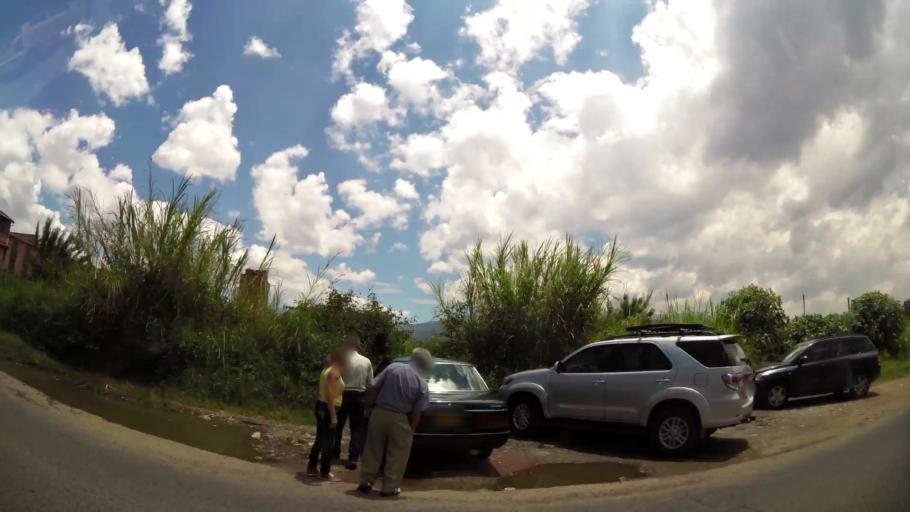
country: CO
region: Antioquia
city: La Estrella
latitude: 6.1619
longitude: -75.6360
